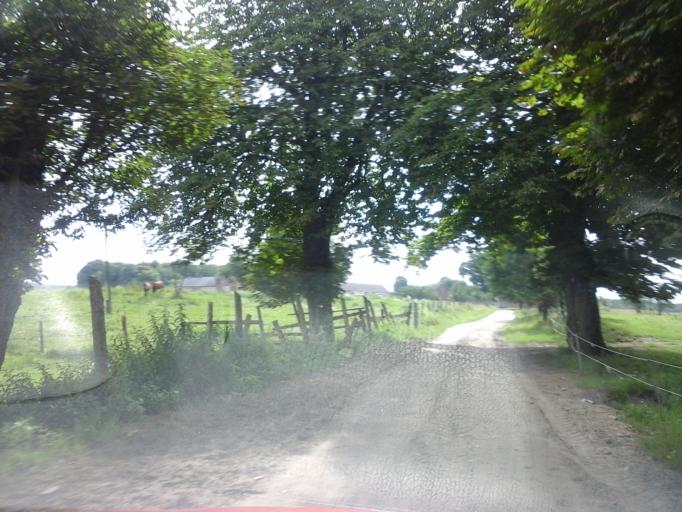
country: PL
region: West Pomeranian Voivodeship
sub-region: Powiat choszczenski
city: Recz
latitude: 53.2430
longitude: 15.6417
